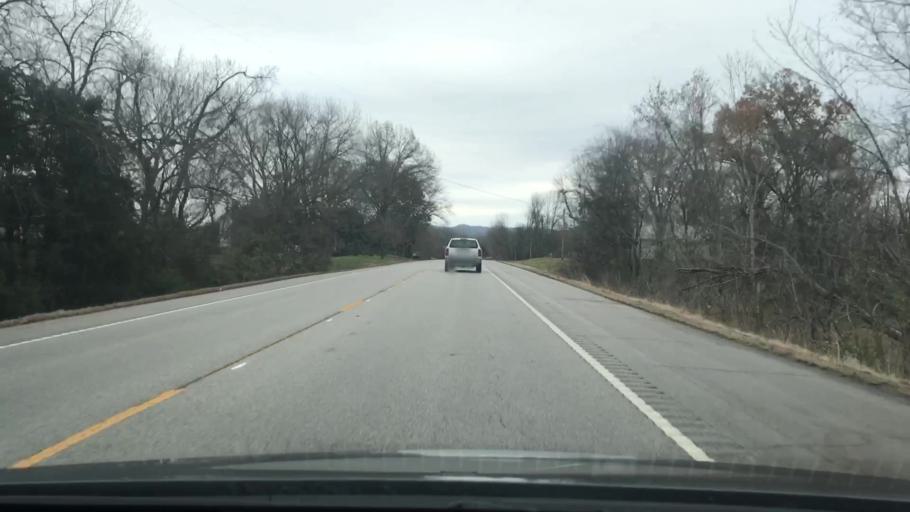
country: US
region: Tennessee
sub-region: Trousdale County
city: Hartsville
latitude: 36.3622
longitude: -86.0613
